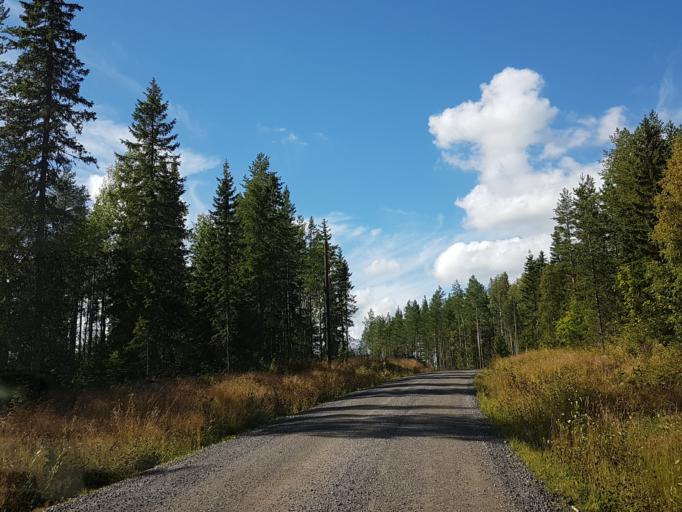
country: SE
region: Vaesterbotten
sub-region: Skelleftea Kommun
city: Burtraesk
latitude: 64.2721
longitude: 20.4876
